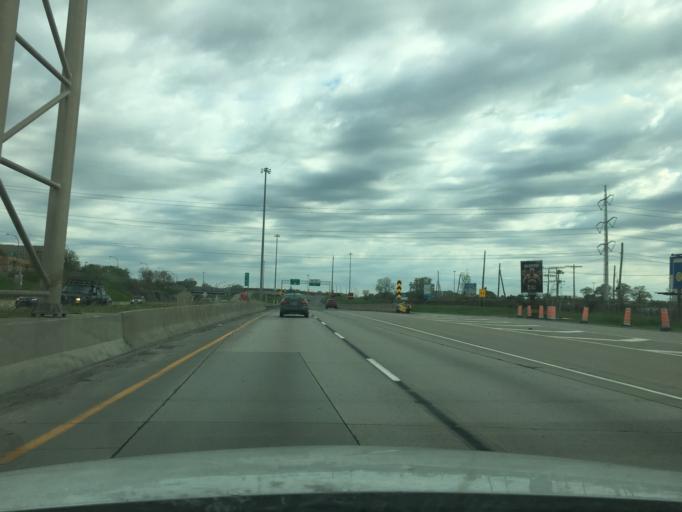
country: CA
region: Quebec
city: Montreal-Est
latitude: 45.5838
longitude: -73.5266
